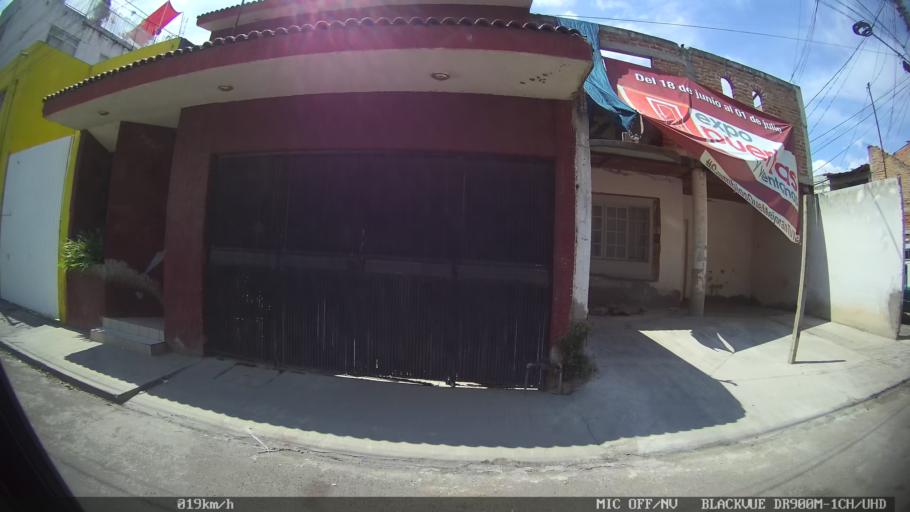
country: MX
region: Jalisco
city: Tonala
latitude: 20.6206
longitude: -103.2523
